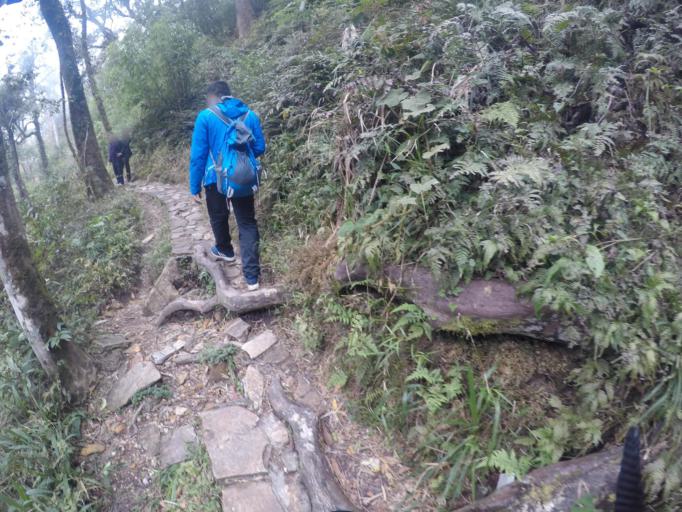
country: VN
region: Lao Cai
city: Sa Pa
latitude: 22.3480
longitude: 103.7721
